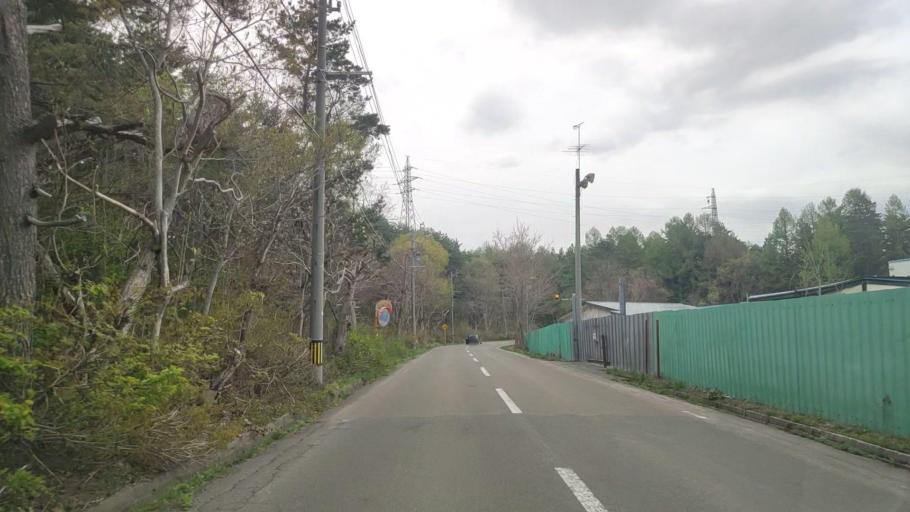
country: JP
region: Aomori
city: Aomori Shi
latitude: 40.7484
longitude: 140.8203
